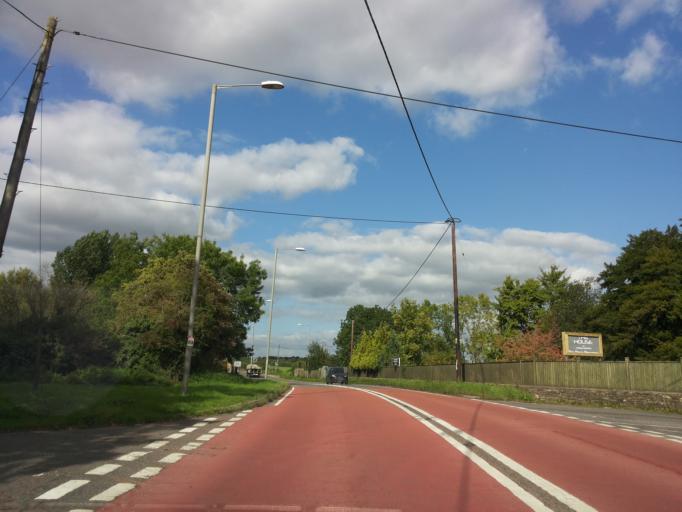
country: GB
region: England
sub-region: Bath and North East Somerset
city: Hinton Charterhouse
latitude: 51.2853
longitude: -2.3001
